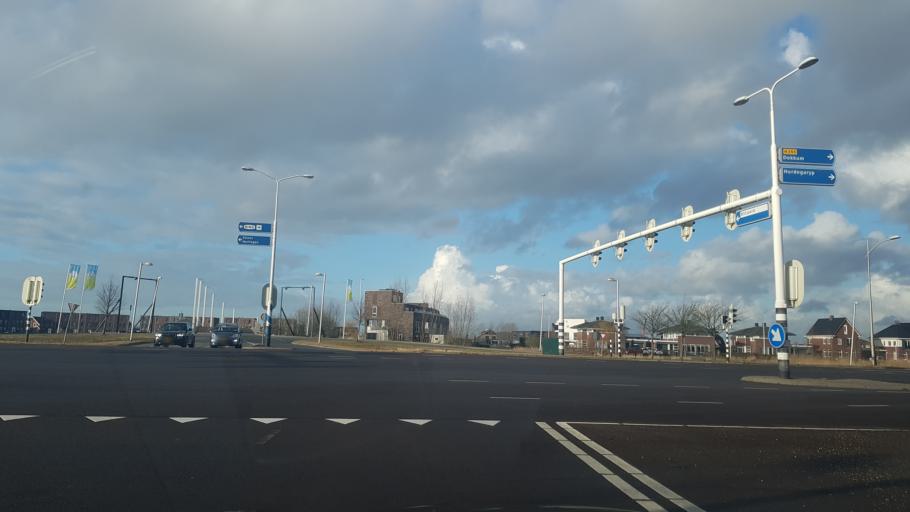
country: NL
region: Friesland
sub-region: Gemeente Leeuwarden
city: Camminghaburen
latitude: 53.2169
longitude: 5.8293
